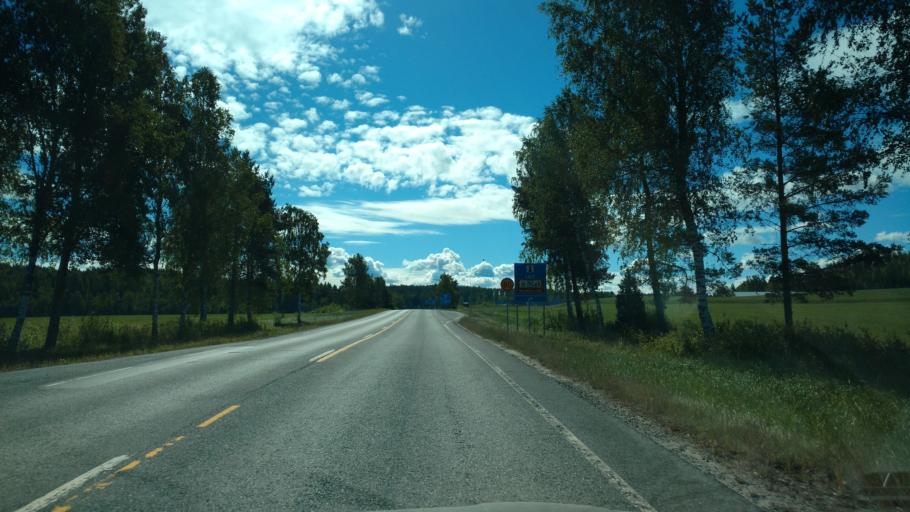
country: FI
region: Varsinais-Suomi
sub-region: Salo
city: Muurla
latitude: 60.3767
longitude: 23.3066
